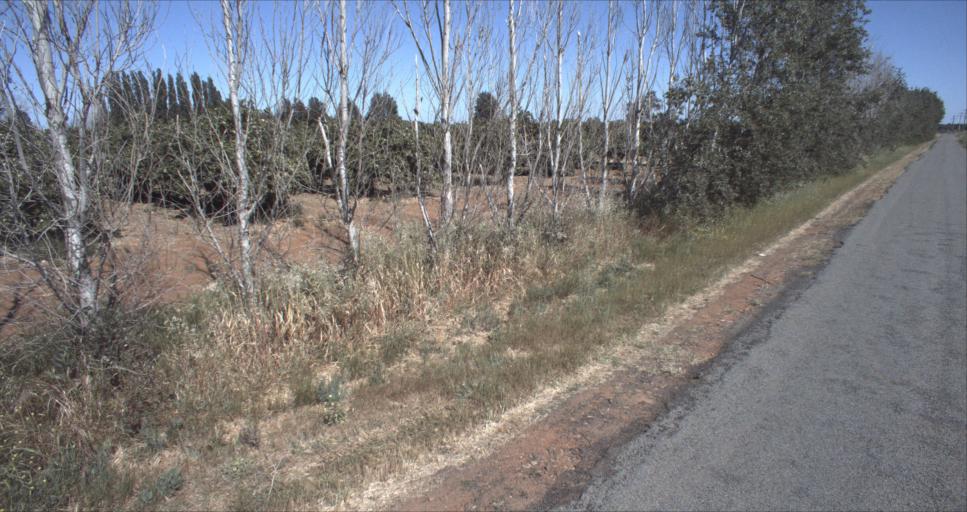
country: AU
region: New South Wales
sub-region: Leeton
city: Leeton
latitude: -34.5422
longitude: 146.3426
